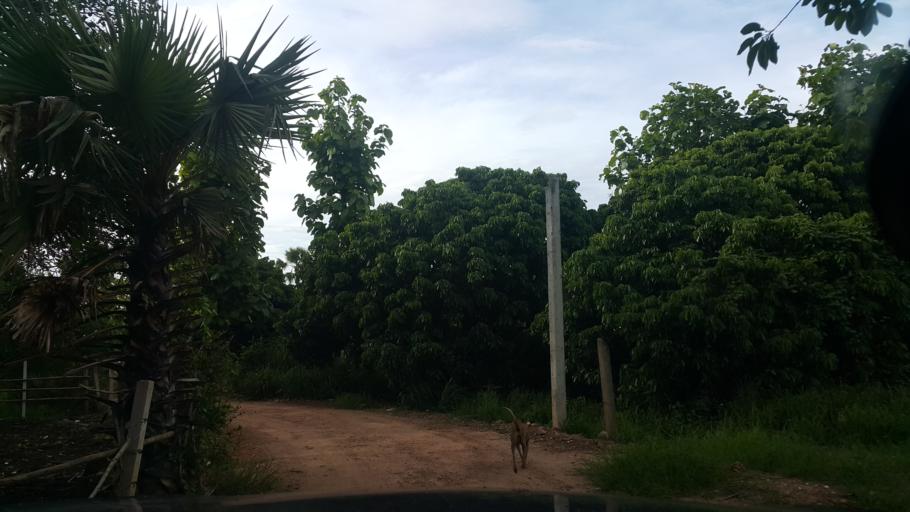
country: TH
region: Chiang Mai
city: Mae On
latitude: 18.7147
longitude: 99.2134
